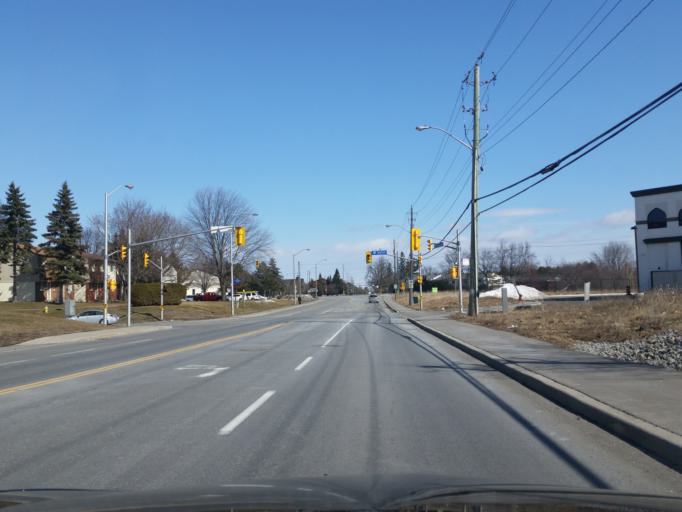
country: CA
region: Ontario
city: Bells Corners
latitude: 45.3112
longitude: -75.8293
